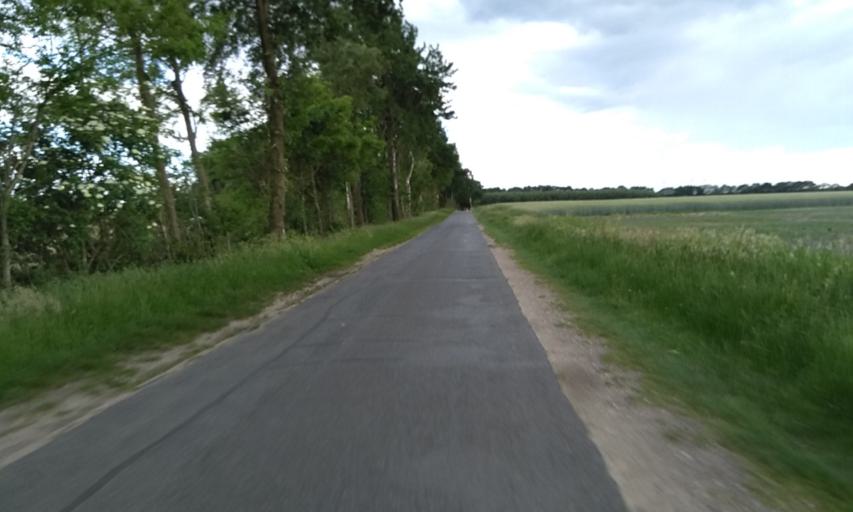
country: DE
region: Lower Saxony
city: Regesbostel
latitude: 53.3885
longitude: 9.6440
